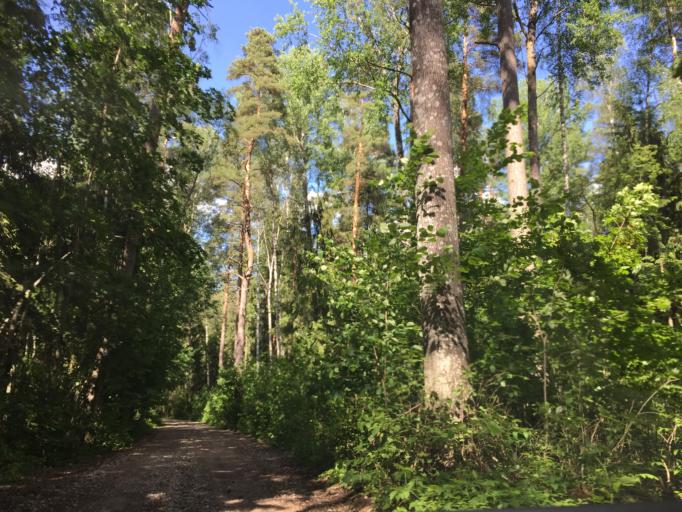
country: LV
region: Engure
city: Smarde
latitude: 56.8173
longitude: 23.3901
